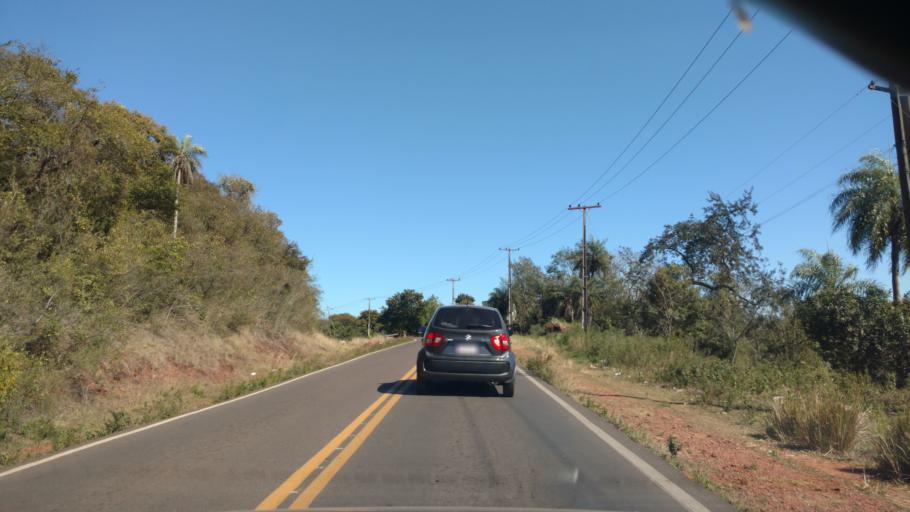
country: PY
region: Paraguari
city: Pirayu
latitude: -25.4942
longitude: -57.2437
